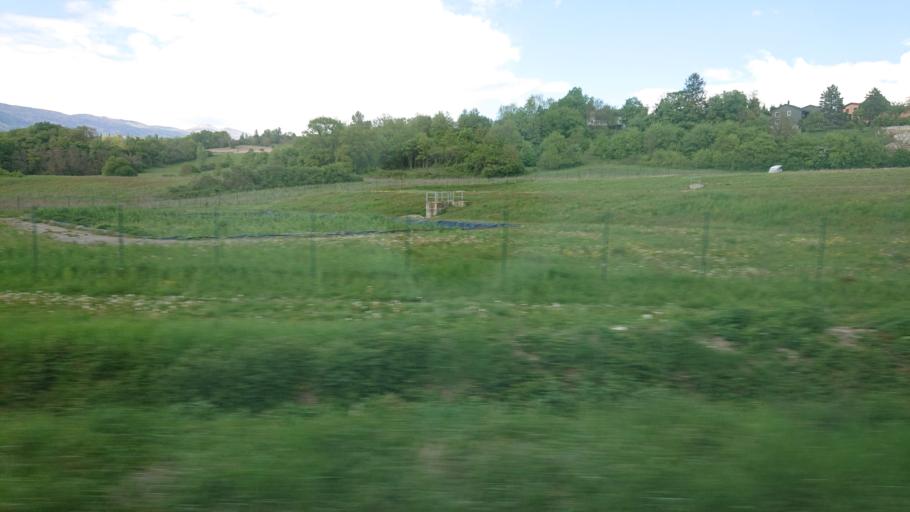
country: CH
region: Geneva
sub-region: Geneva
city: Chancy
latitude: 46.1335
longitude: 5.9481
